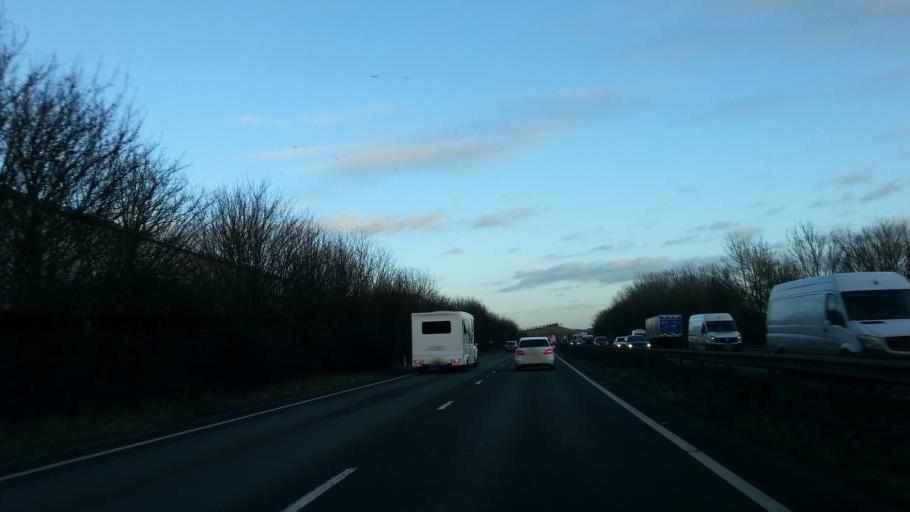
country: GB
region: England
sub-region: Northamptonshire
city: Thrapston
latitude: 52.3923
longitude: -0.5751
